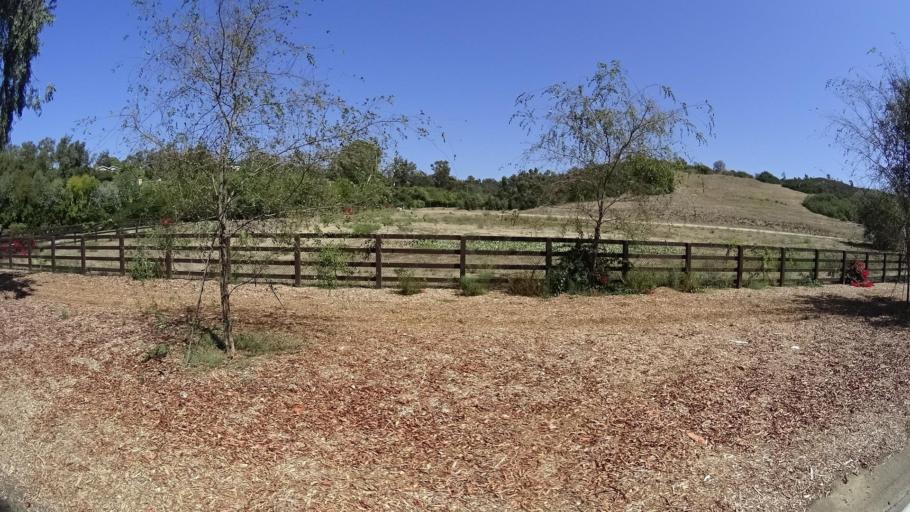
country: US
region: California
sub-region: San Diego County
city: Rancho Santa Fe
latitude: 33.0119
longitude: -117.2284
